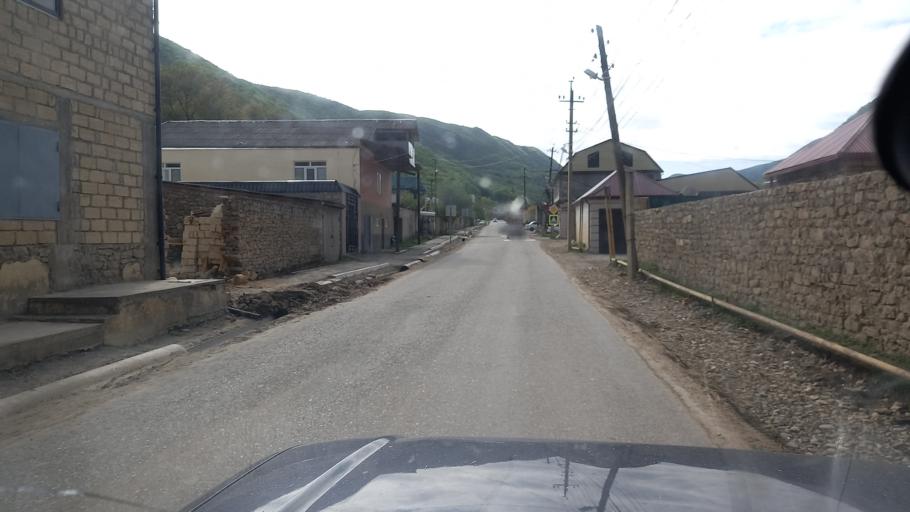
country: RU
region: Dagestan
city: Khuchni
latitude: 41.9622
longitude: 47.9556
